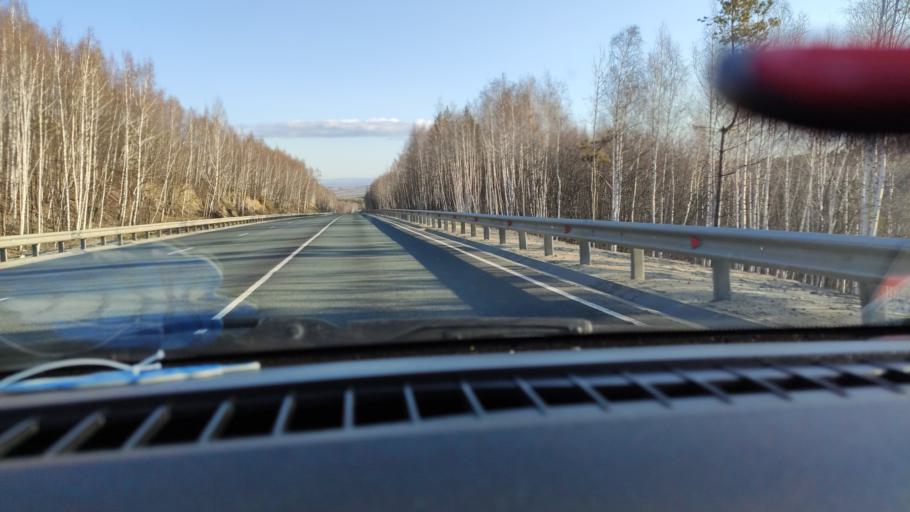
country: RU
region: Saratov
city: Khvalynsk
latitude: 52.5006
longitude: 48.0149
